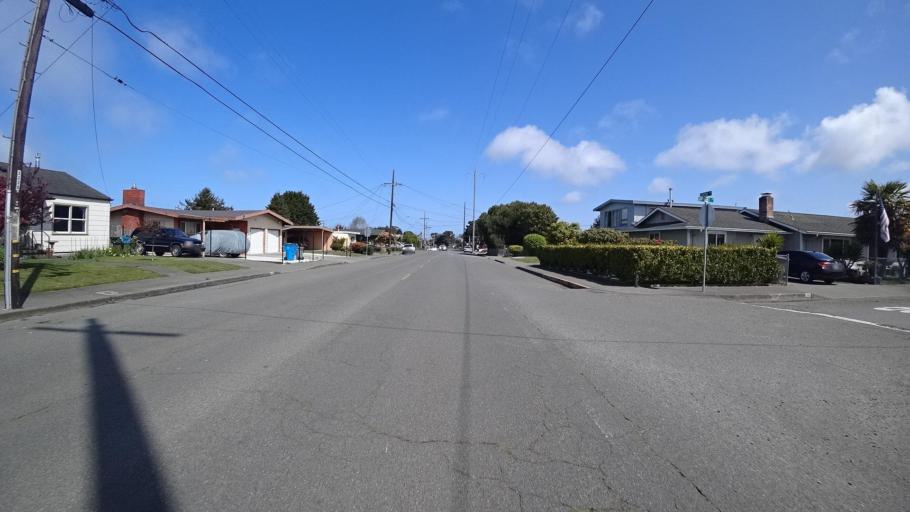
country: US
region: California
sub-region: Humboldt County
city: Bayview
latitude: 40.7792
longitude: -124.1803
